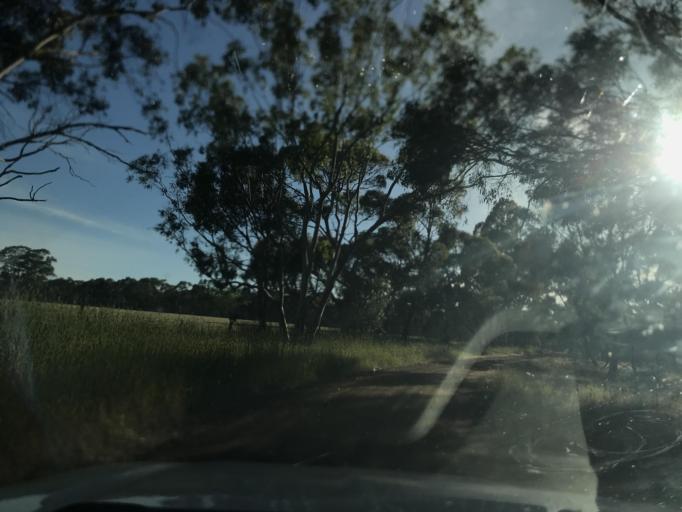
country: AU
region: South Australia
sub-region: Wattle Range
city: Penola
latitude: -37.1190
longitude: 141.4425
